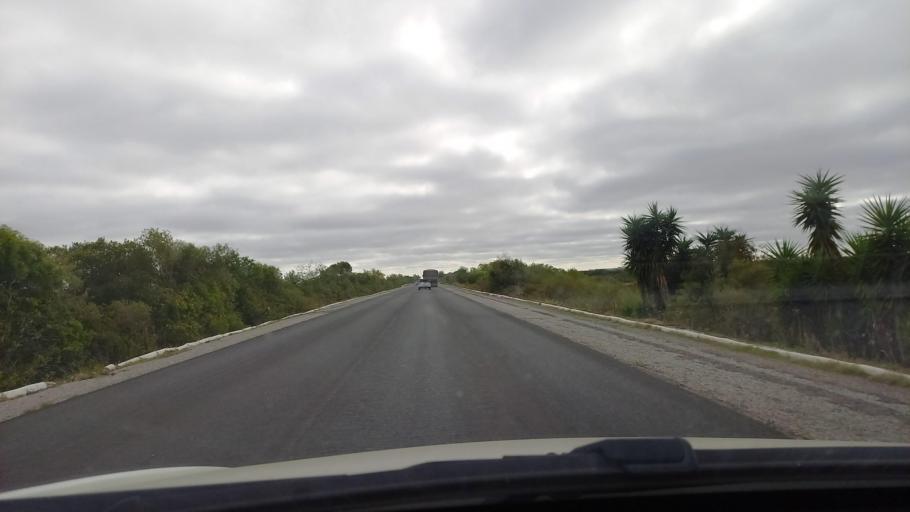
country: BR
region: Rio Grande do Sul
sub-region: Dom Pedrito
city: Dom Pedrito
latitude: -30.9526
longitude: -54.7005
